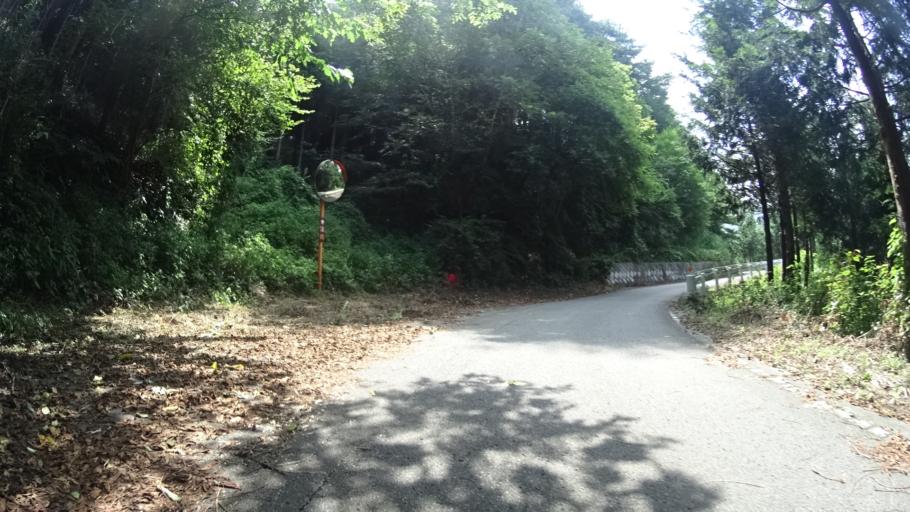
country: JP
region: Yamanashi
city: Nirasaki
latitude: 35.8850
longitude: 138.4780
